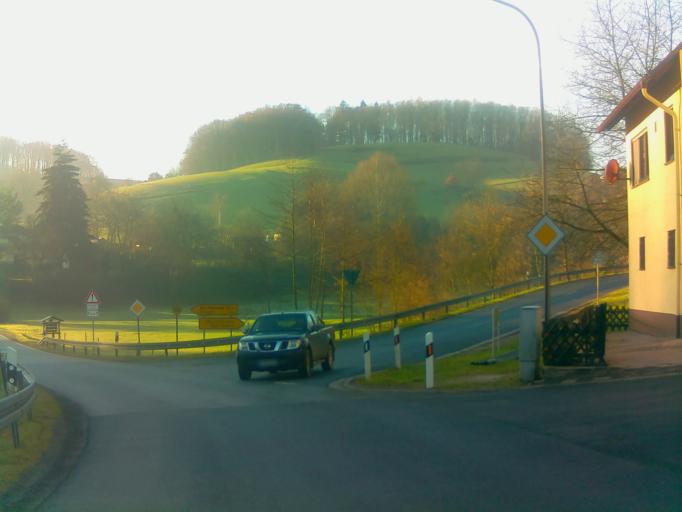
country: DE
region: Hesse
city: Reichelsheim
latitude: 49.6861
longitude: 8.8604
